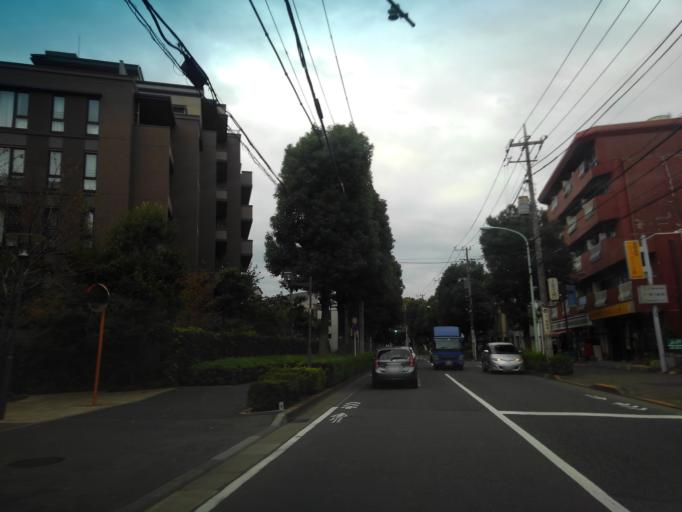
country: JP
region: Tokyo
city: Chofugaoka
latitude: 35.6612
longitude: 139.5412
